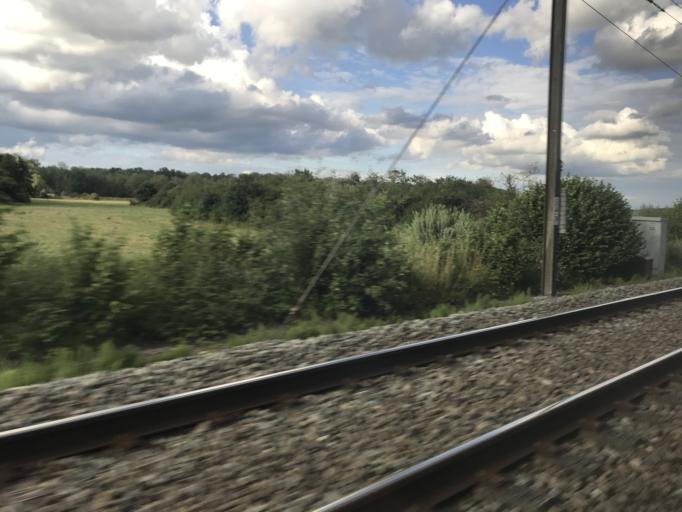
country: FR
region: Champagne-Ardenne
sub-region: Departement des Ardennes
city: Douzy
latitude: 49.6727
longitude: 5.0107
